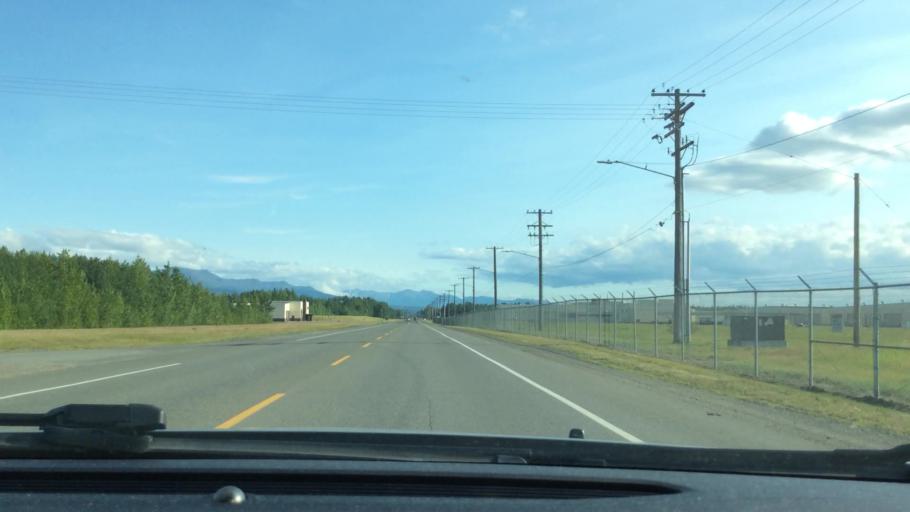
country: US
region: Alaska
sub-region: Anchorage Municipality
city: Anchorage
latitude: 61.2501
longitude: -149.7791
